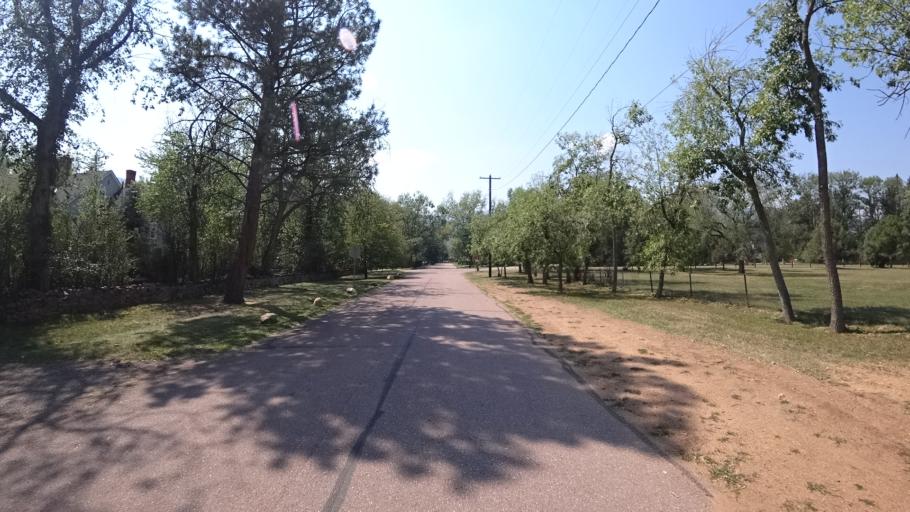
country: US
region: Colorado
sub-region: El Paso County
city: Colorado Springs
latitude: 38.7903
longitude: -104.8439
